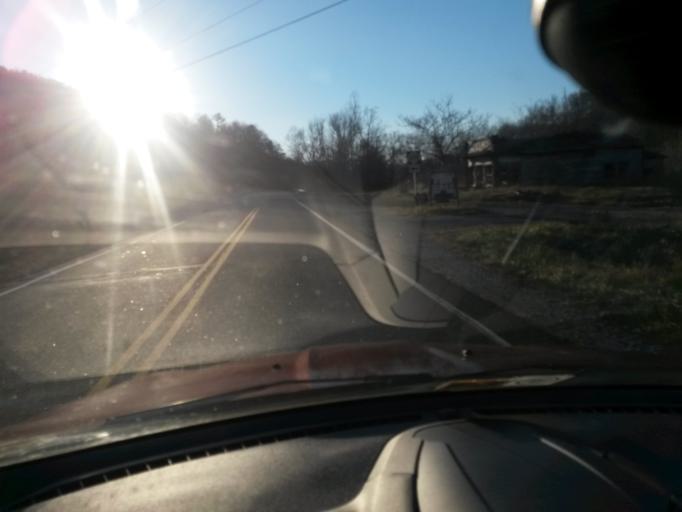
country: US
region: Virginia
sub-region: City of Buena Vista
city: Buena Vista
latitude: 37.6808
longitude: -79.2228
